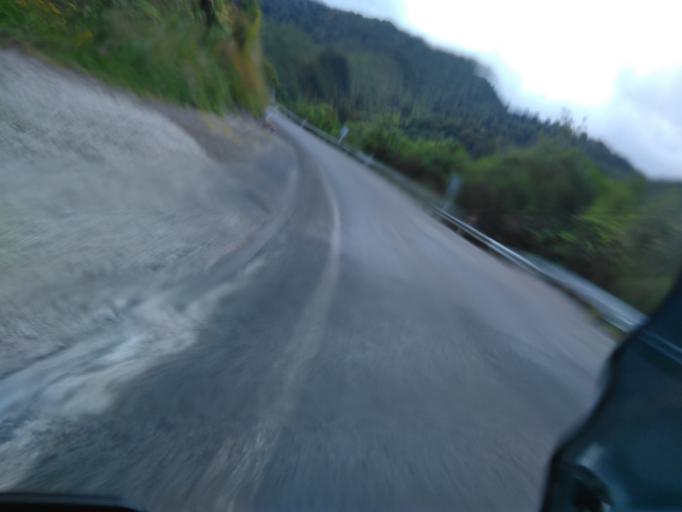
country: NZ
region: Bay of Plenty
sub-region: Opotiki District
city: Opotiki
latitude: -38.3452
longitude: 177.4479
